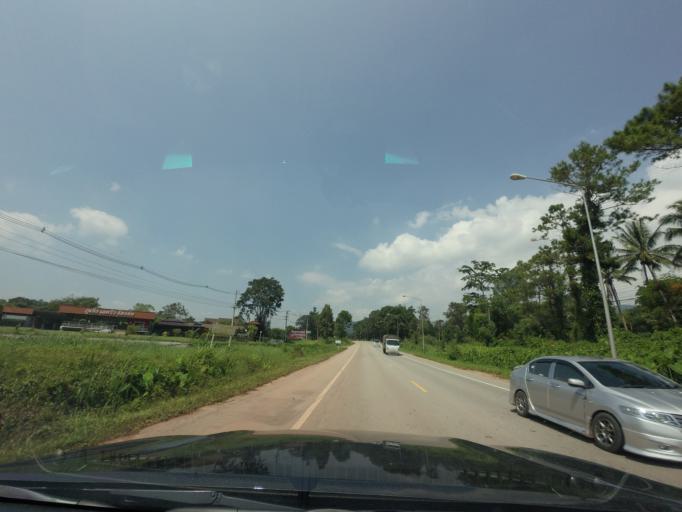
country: TH
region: Loei
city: Phu Ruea
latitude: 17.4577
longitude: 101.3873
